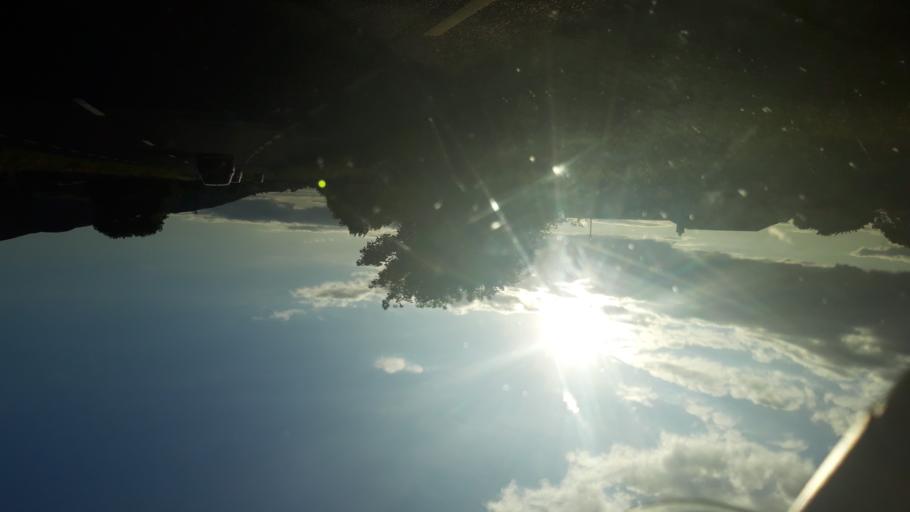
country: IE
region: Leinster
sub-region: Lu
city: Carlingford
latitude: 53.9972
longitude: -6.2298
